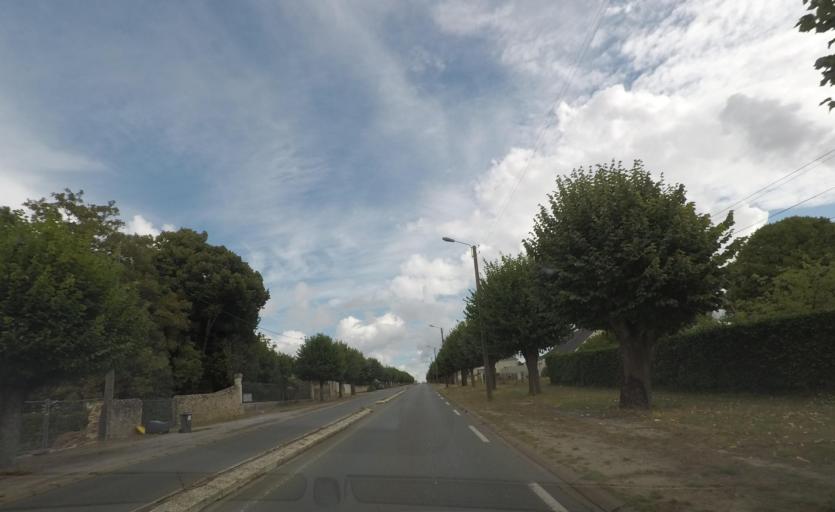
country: FR
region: Pays de la Loire
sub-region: Departement de Maine-et-Loire
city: Seiches-sur-le-Loir
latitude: 47.5749
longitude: -0.3540
